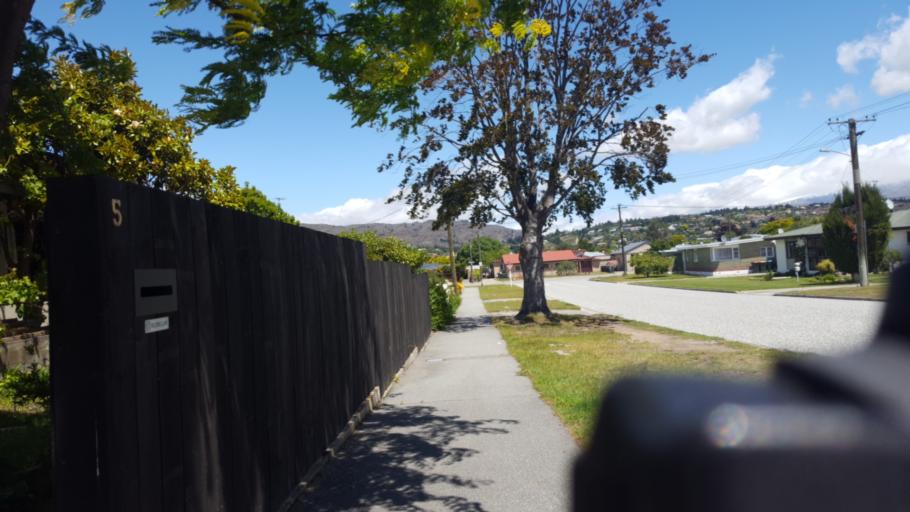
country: NZ
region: Otago
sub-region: Queenstown-Lakes District
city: Wanaka
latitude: -45.2478
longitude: 169.3909
